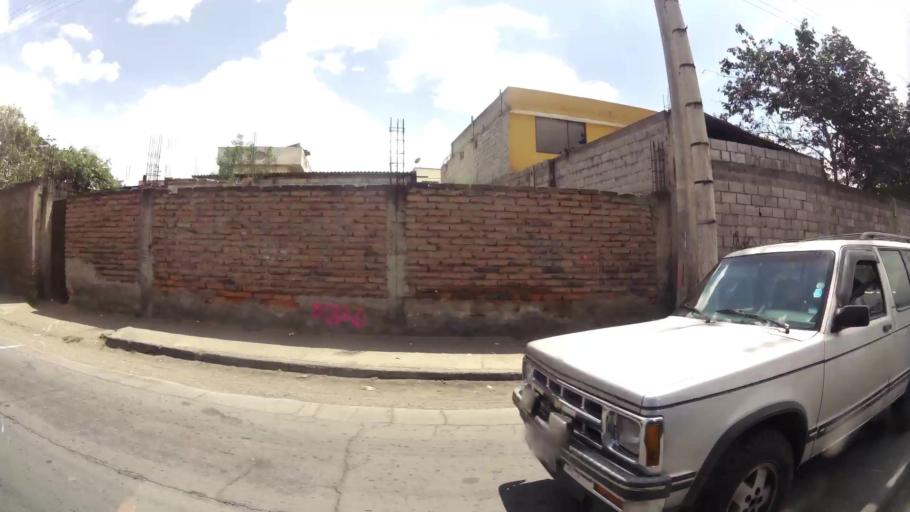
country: EC
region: Pichincha
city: Quito
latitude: -0.1025
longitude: -78.4201
